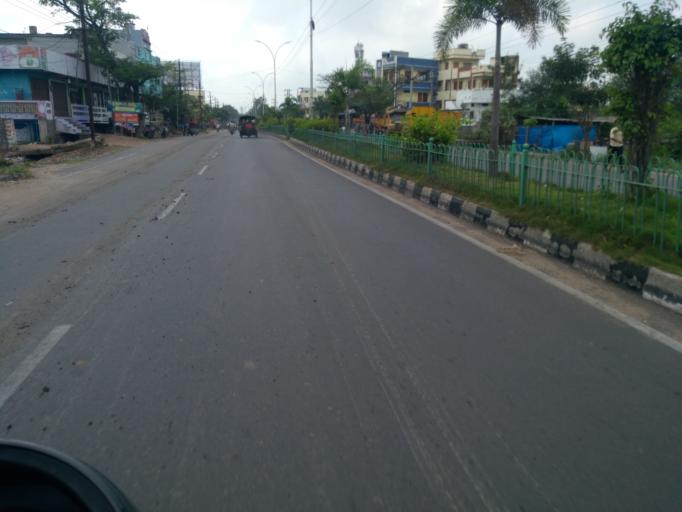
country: IN
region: Telangana
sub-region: Warangal
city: Warangal
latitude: 17.9562
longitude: 79.6010
